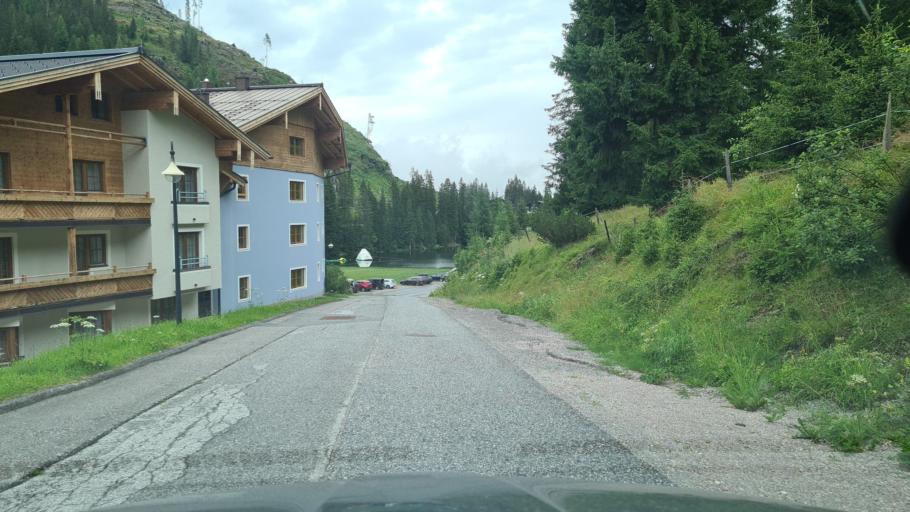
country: AT
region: Salzburg
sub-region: Politischer Bezirk Sankt Johann im Pongau
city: Untertauern
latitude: 47.2941
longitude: 13.4576
